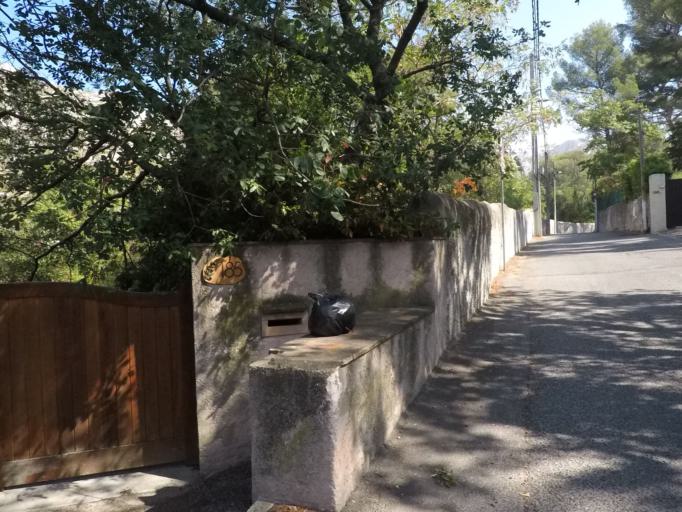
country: FR
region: Provence-Alpes-Cote d'Azur
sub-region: Departement des Bouches-du-Rhone
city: Marseille 09
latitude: 43.2556
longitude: 5.4346
